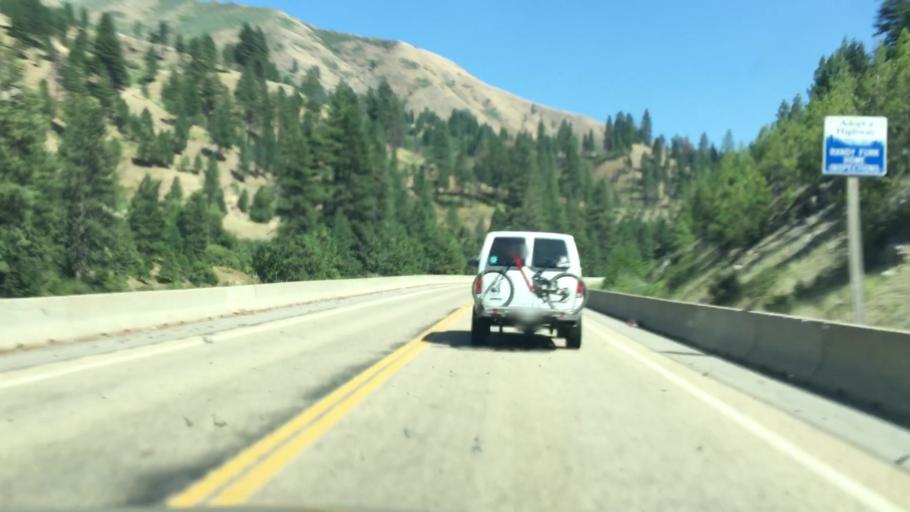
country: US
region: Idaho
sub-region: Boise County
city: Idaho City
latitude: 44.1173
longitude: -116.1098
